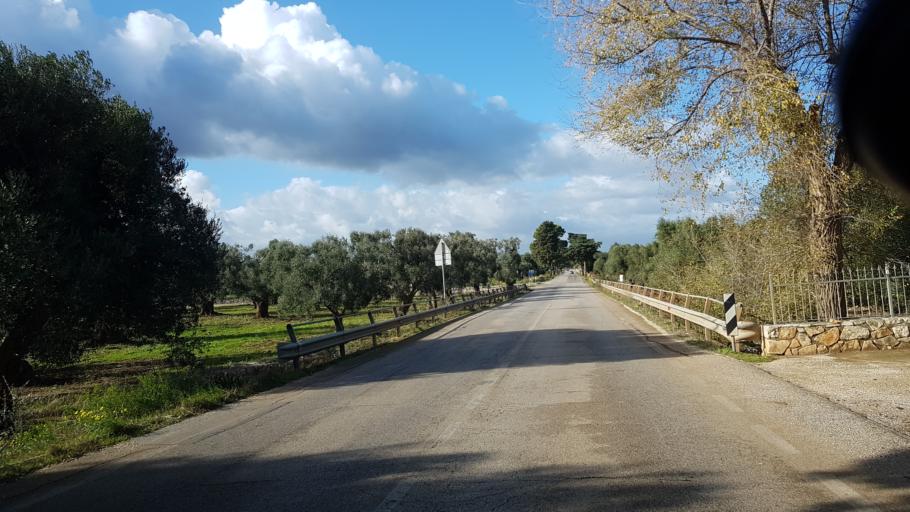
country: IT
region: Apulia
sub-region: Provincia di Brindisi
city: Pezze di Greco
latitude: 40.7969
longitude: 17.4483
